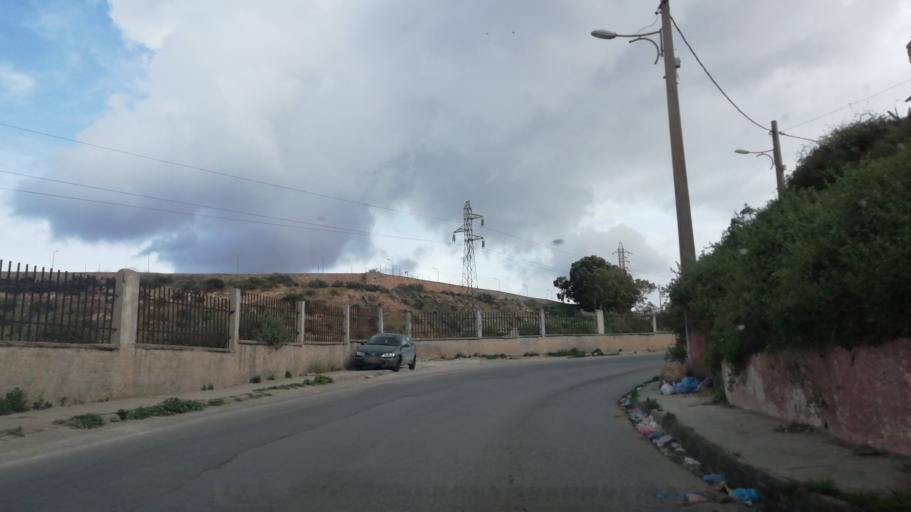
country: DZ
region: Oran
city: Oran
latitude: 35.6932
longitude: -0.6589
